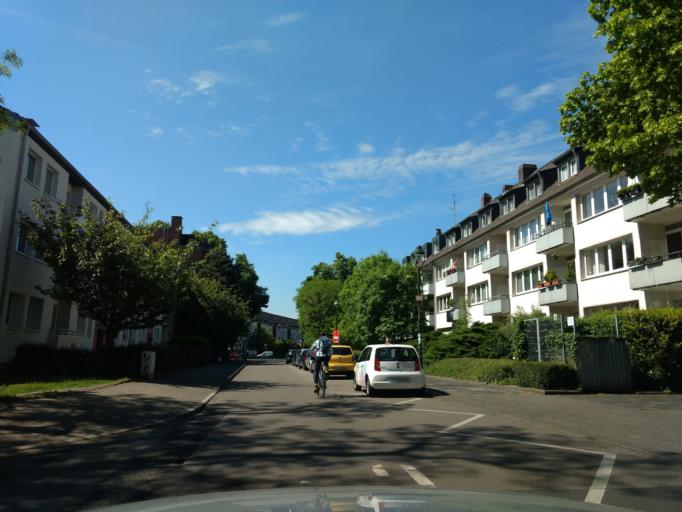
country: DE
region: North Rhine-Westphalia
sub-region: Regierungsbezirk Dusseldorf
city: Dusseldorf
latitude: 51.2486
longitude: 6.8076
